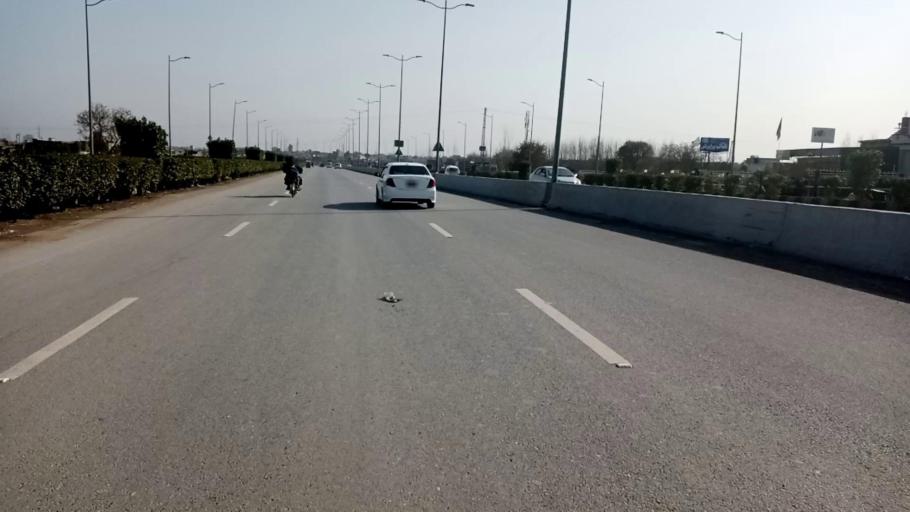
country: PK
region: Khyber Pakhtunkhwa
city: Peshawar
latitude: 34.0342
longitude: 71.5414
